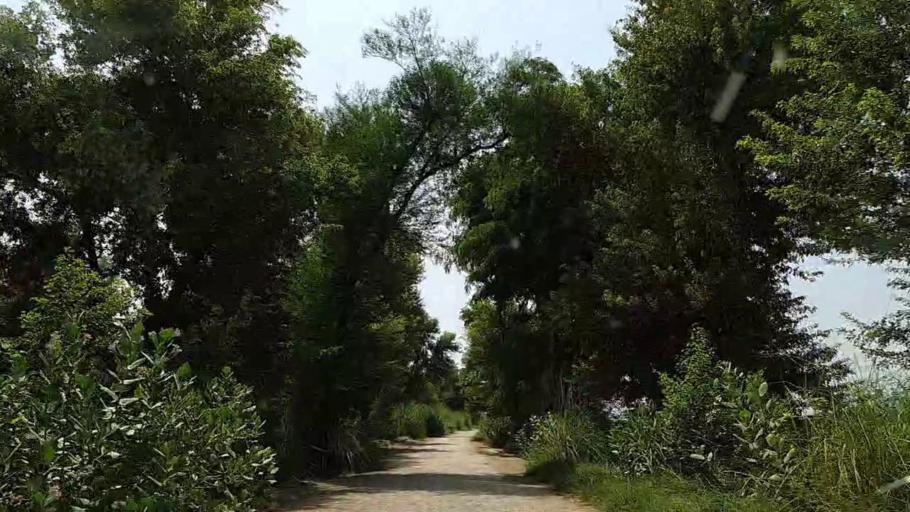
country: PK
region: Sindh
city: Adilpur
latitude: 27.9313
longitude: 69.3865
